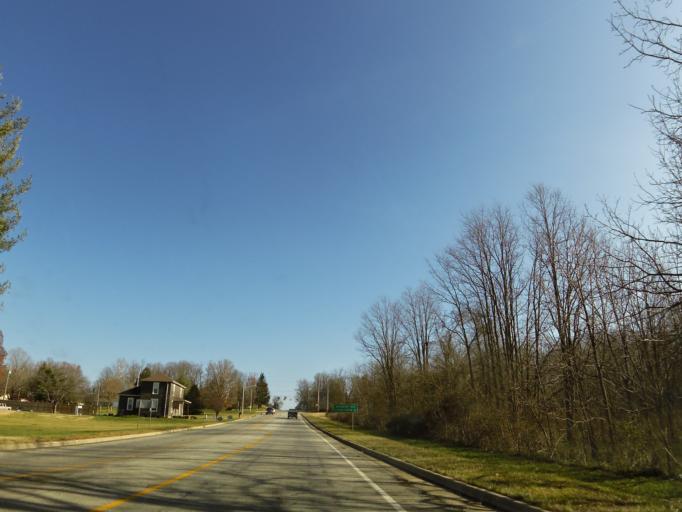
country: US
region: Indiana
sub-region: Fayette County
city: Connersville
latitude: 39.6381
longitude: -85.1695
